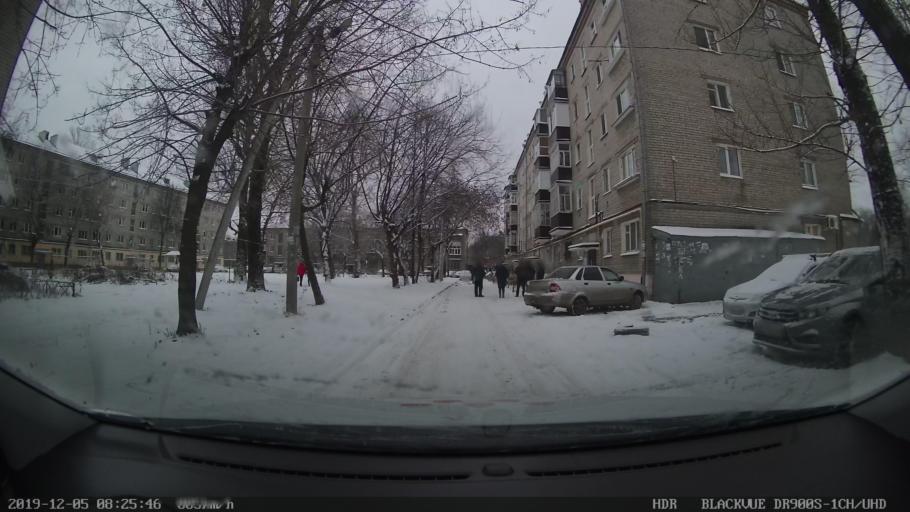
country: RU
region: Tatarstan
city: Staroye Arakchino
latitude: 55.8757
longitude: 49.0220
